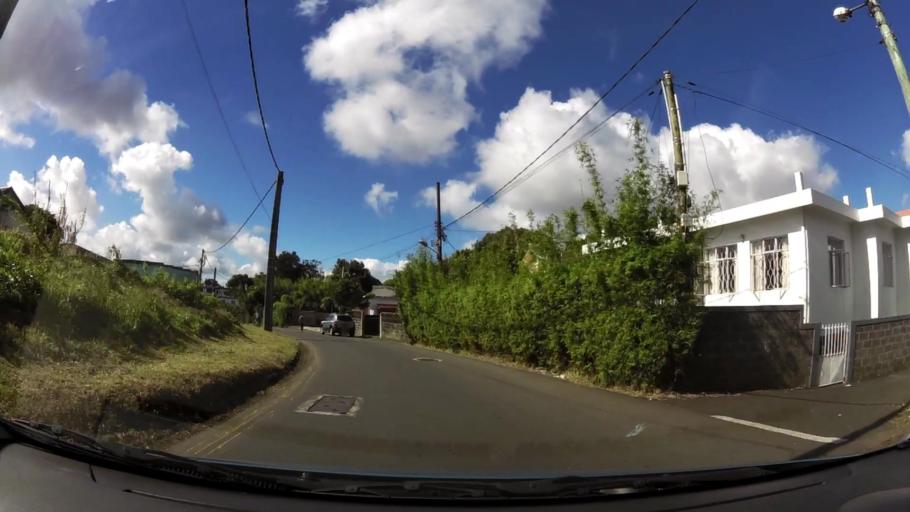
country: MU
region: Plaines Wilhems
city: Curepipe
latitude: -20.3267
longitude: 57.5291
